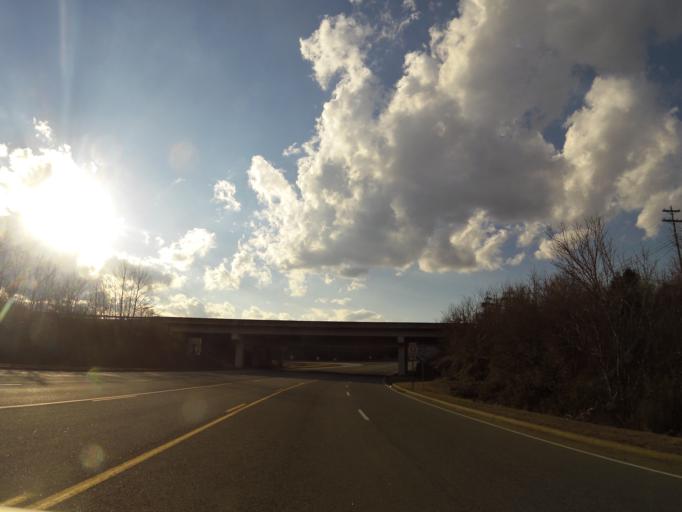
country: US
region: Tennessee
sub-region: Smith County
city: South Carthage
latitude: 36.2354
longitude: -85.9444
